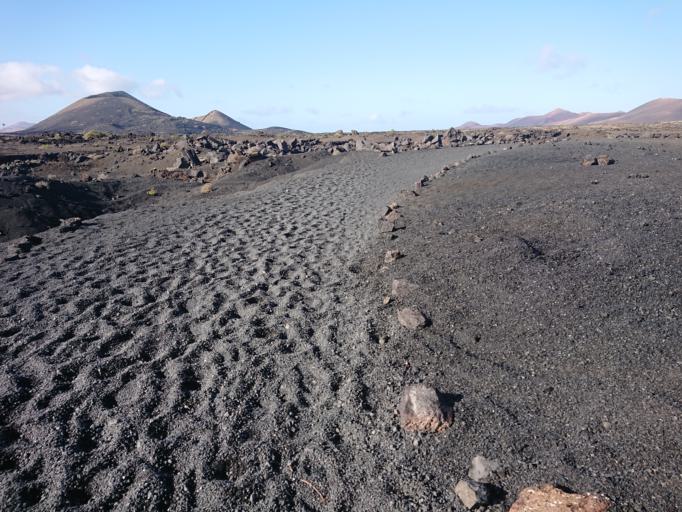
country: ES
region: Canary Islands
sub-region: Provincia de Las Palmas
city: Tias
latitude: 28.9887
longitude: -13.6948
